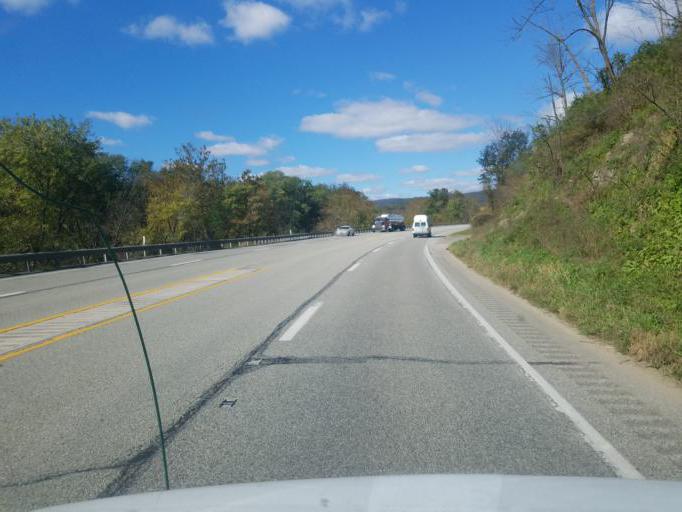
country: US
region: Pennsylvania
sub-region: Bedford County
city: Everett
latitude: 40.0121
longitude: -78.3952
